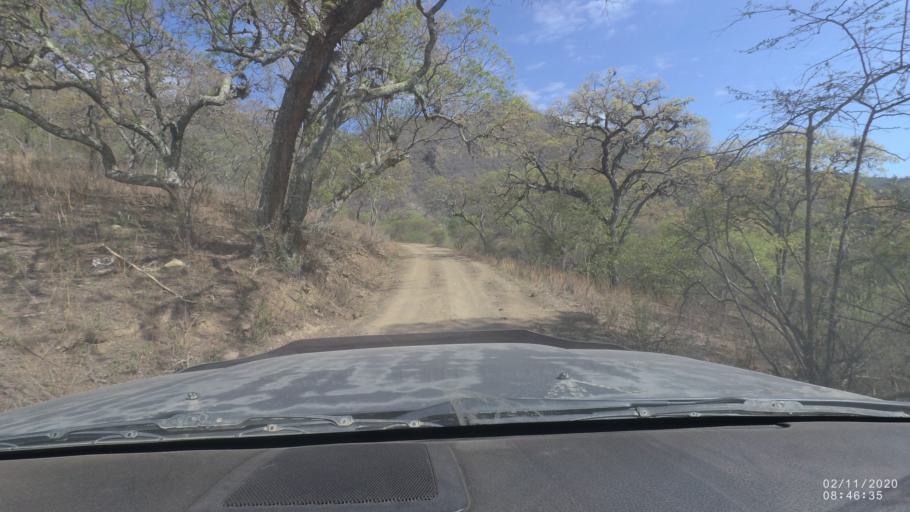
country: BO
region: Chuquisaca
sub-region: Provincia Zudanez
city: Mojocoya
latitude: -18.5637
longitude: -64.5456
